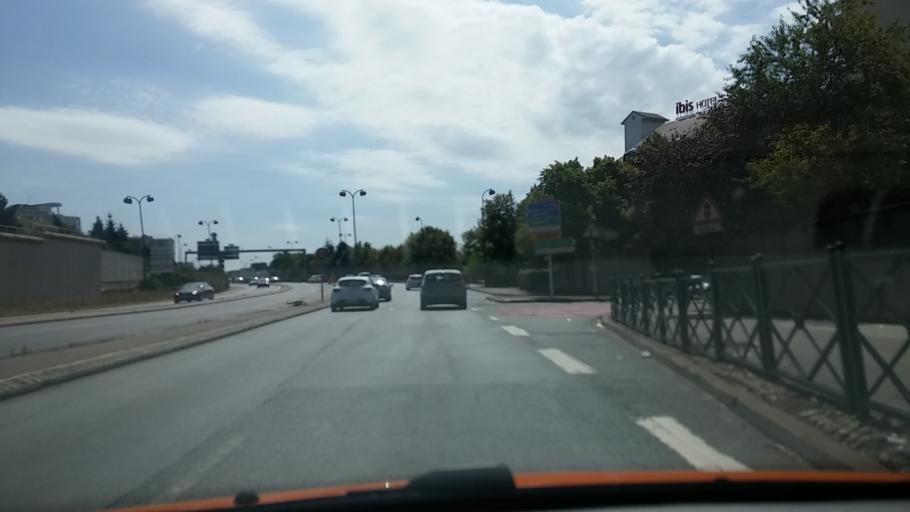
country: FR
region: Ile-de-France
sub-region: Departement du Val-de-Marne
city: Nogent-sur-Marne
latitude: 48.8342
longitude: 2.4930
